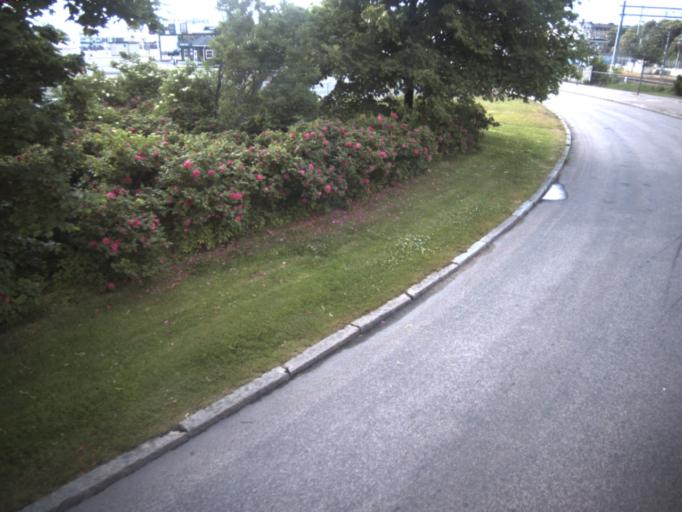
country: SE
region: Skane
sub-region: Helsingborg
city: Helsingborg
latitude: 56.0399
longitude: 12.6976
